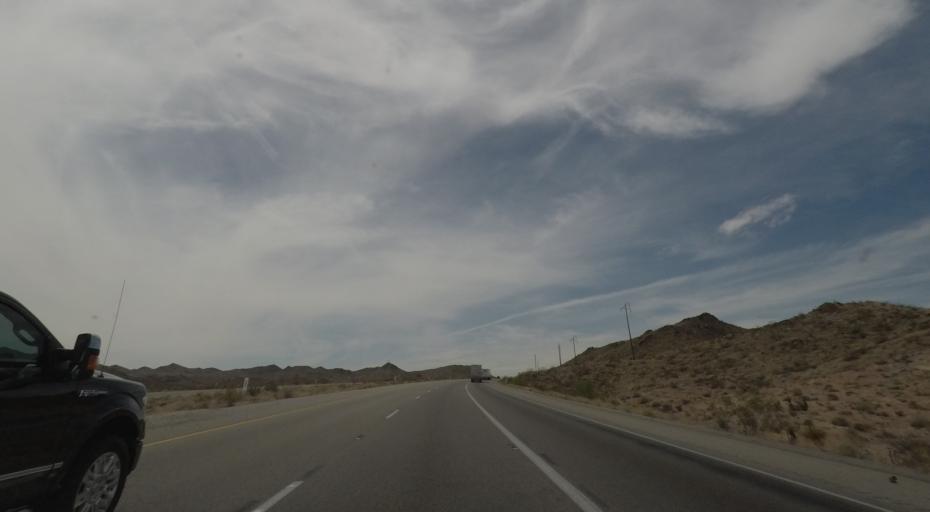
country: US
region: California
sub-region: San Bernardino County
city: Needles
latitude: 34.8296
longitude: -115.0276
